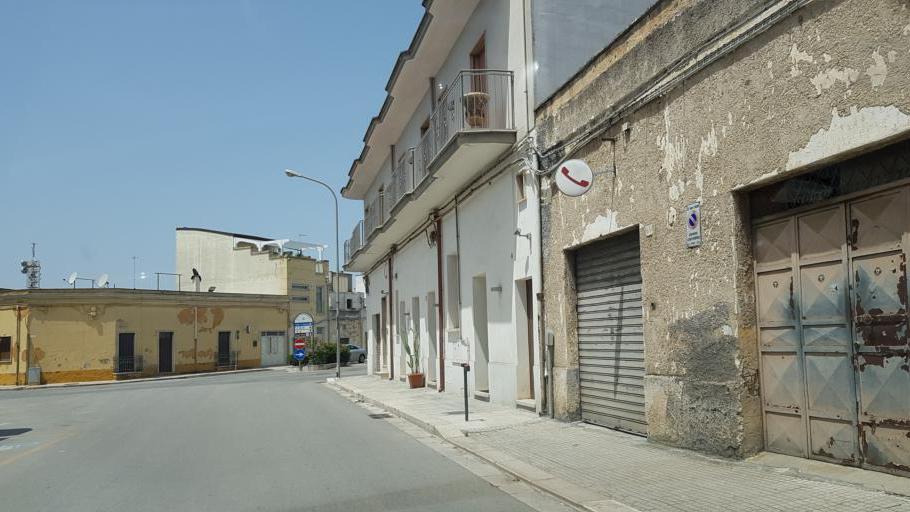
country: IT
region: Apulia
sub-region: Provincia di Brindisi
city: Mesagne
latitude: 40.5558
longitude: 17.8103
